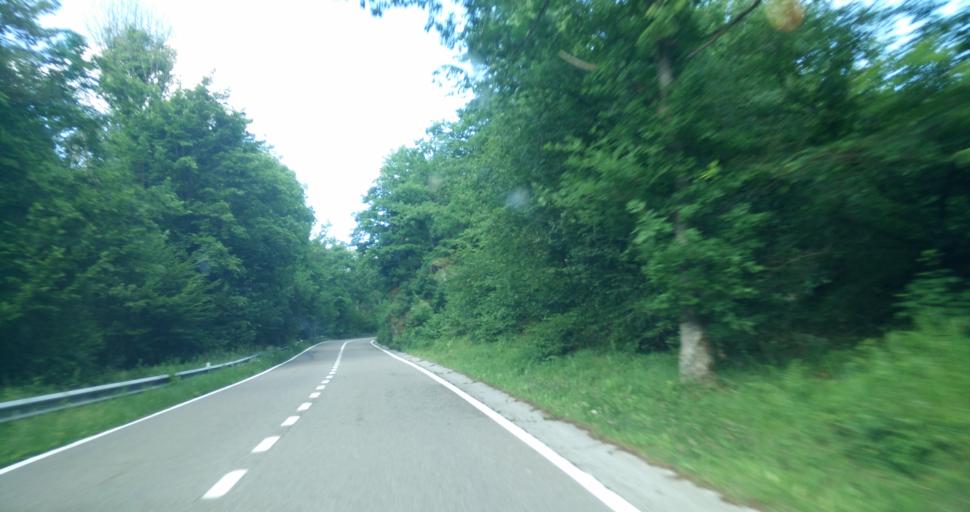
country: BE
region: Wallonia
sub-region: Province du Luxembourg
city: La Roche-en-Ardenne
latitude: 50.1740
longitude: 5.6325
